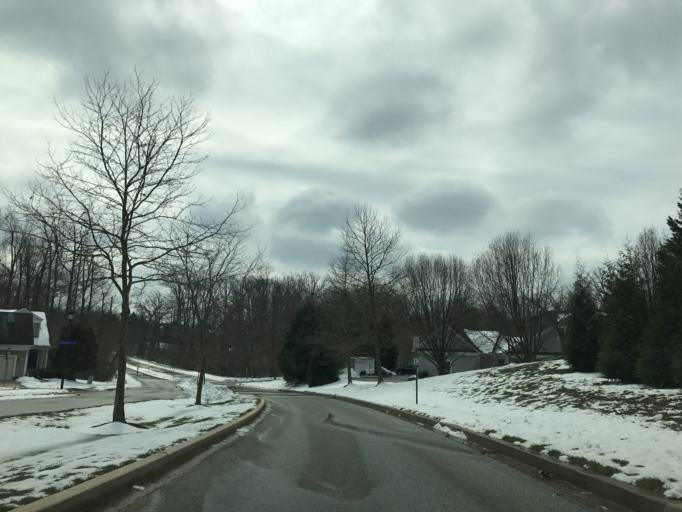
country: US
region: Maryland
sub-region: Harford County
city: Bel Air North
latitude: 39.5686
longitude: -76.3722
